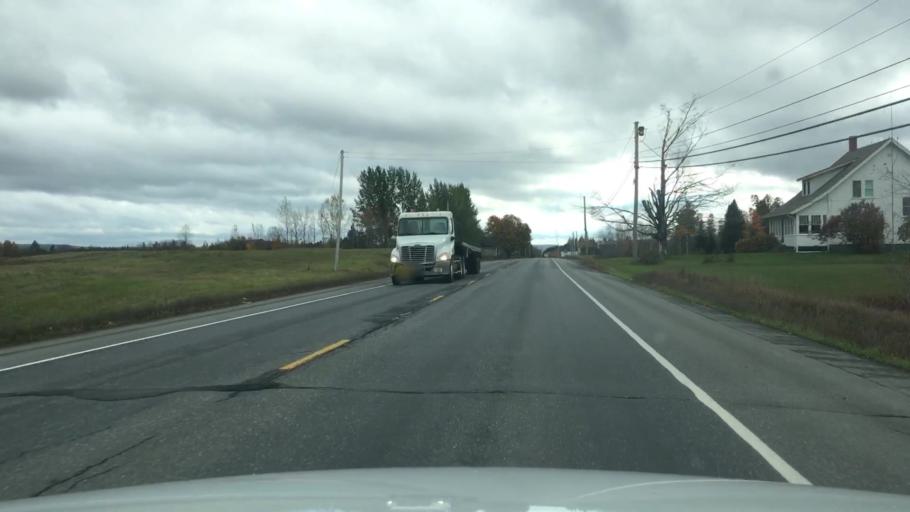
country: US
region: Maine
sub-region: Aroostook County
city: Houlton
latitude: 46.1836
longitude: -67.8412
